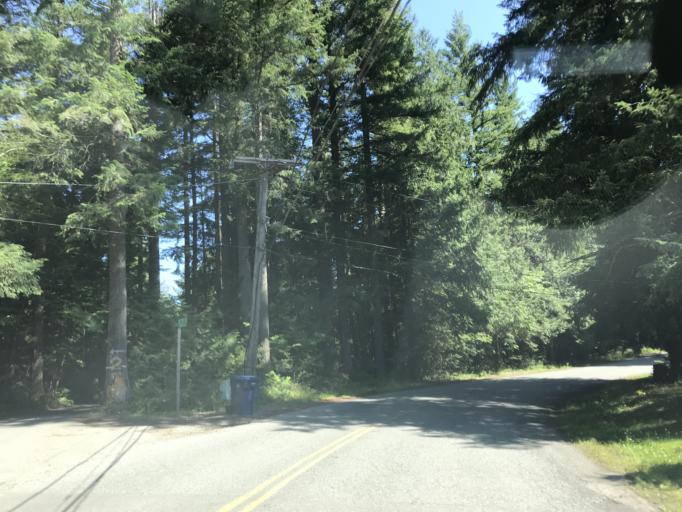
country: US
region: Washington
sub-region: King County
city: Ravensdale
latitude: 47.3711
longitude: -121.8801
